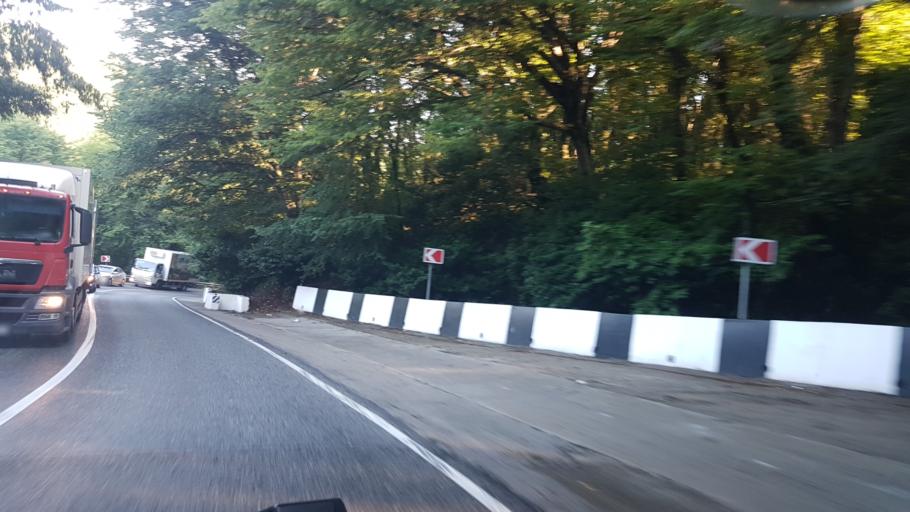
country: RU
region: Krasnodarskiy
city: Gornoye Loo
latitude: 43.6695
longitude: 39.6214
